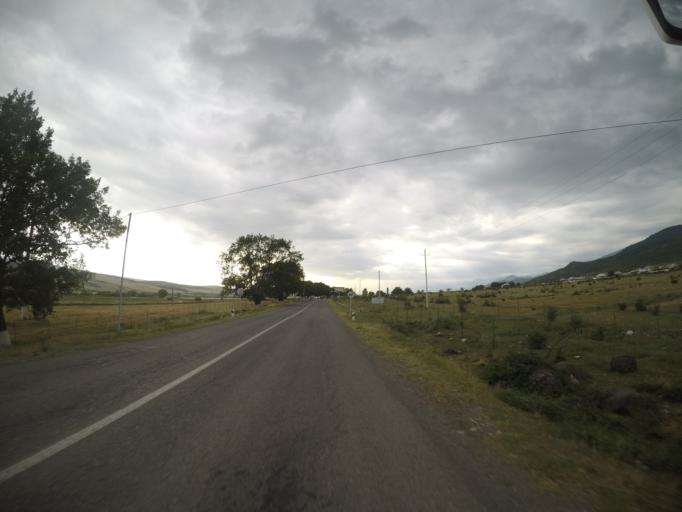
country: AZ
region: Ismayilli
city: Ismayilli
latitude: 40.7579
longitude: 48.2193
